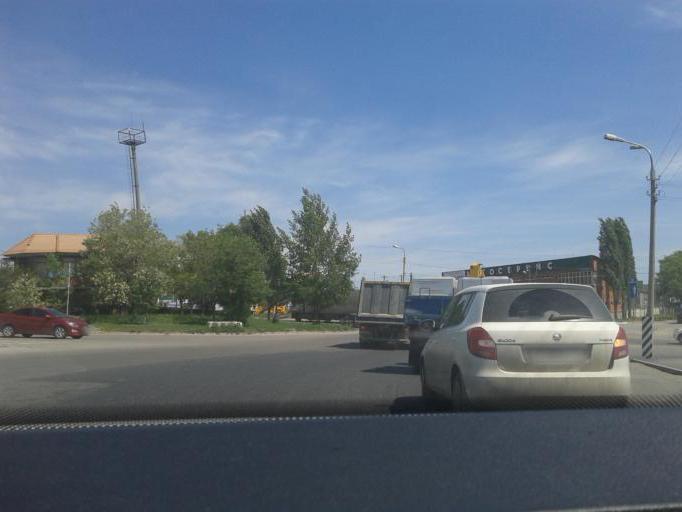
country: RU
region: Volgograd
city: Gorodishche
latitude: 48.7758
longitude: 44.5197
